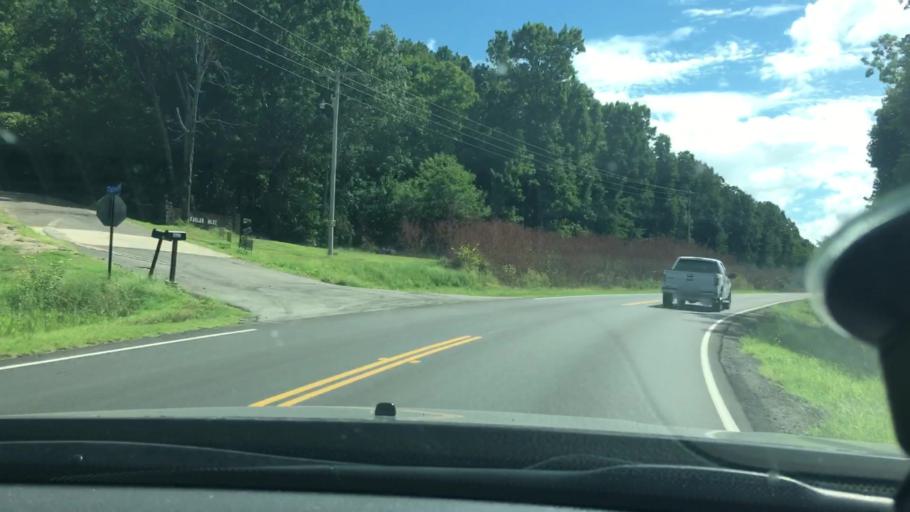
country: US
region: Oklahoma
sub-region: Sequoyah County
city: Vian
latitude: 35.6562
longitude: -94.9514
